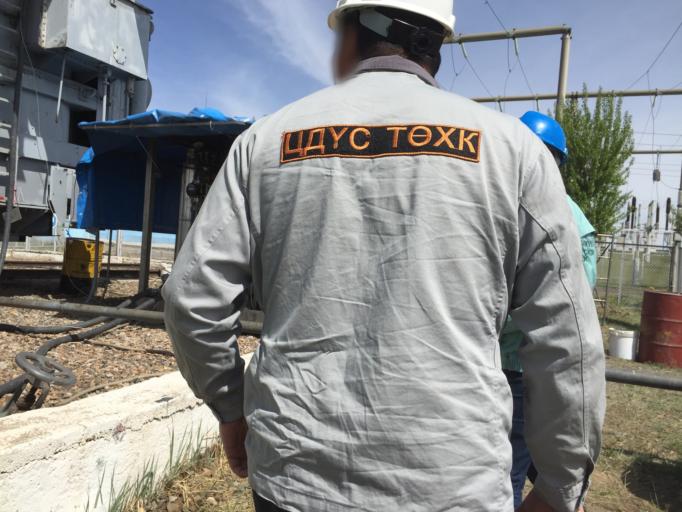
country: MN
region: Darhan Uul
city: Darhan
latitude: 49.3968
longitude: 105.9470
